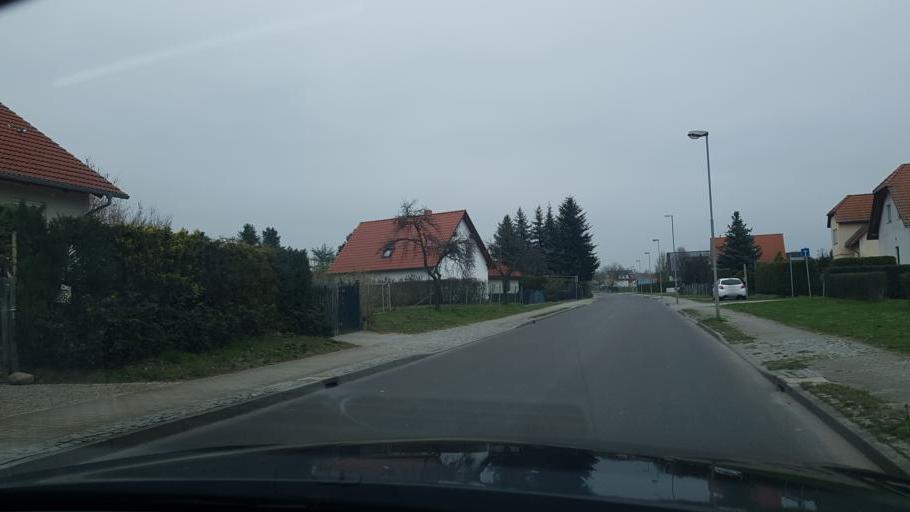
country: DE
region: Brandenburg
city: Mittenwalde
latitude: 52.2858
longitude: 13.5425
